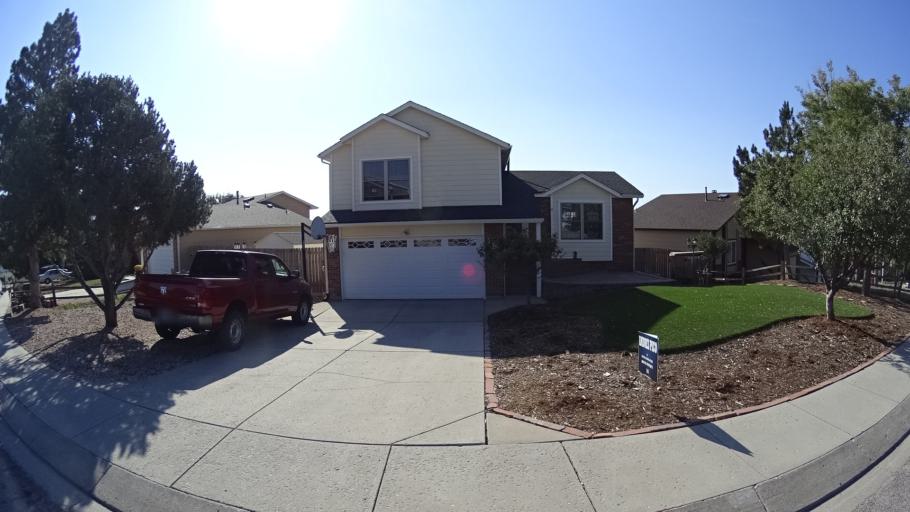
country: US
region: Colorado
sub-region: El Paso County
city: Cimarron Hills
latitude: 38.8901
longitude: -104.7249
